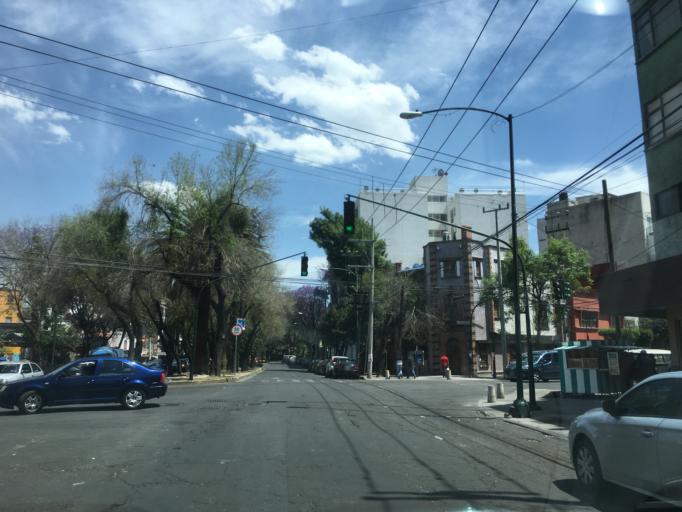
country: MX
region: Mexico City
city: Benito Juarez
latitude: 19.3935
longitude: -99.1528
